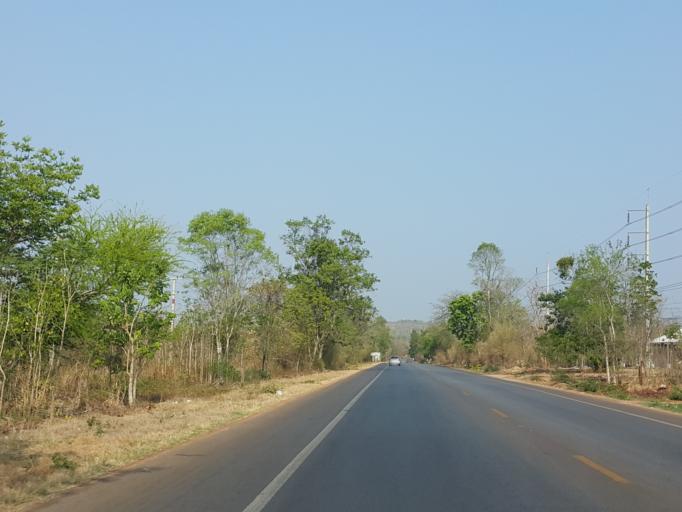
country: TH
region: Kanchanaburi
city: Sai Yok
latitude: 14.0976
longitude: 99.2427
